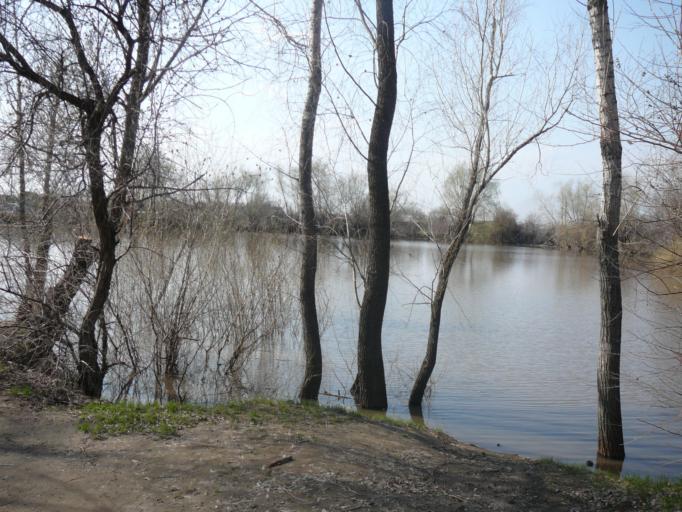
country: RU
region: Saratov
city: Engel's
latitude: 51.4604
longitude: 46.1725
